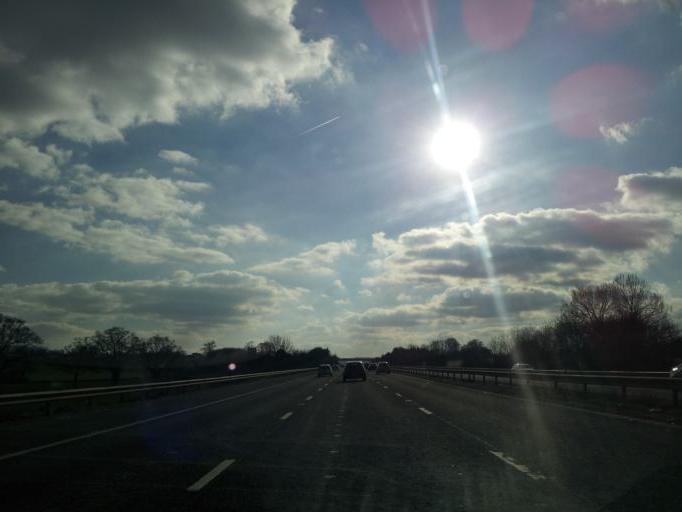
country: GB
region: England
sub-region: Somerset
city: Taunton
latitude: 50.9892
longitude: -3.1008
